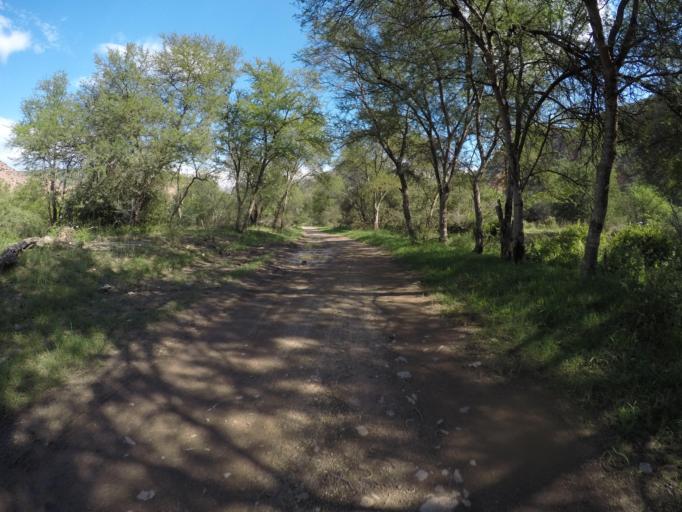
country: ZA
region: Eastern Cape
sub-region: Cacadu District Municipality
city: Kareedouw
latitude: -33.6650
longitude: 24.3876
